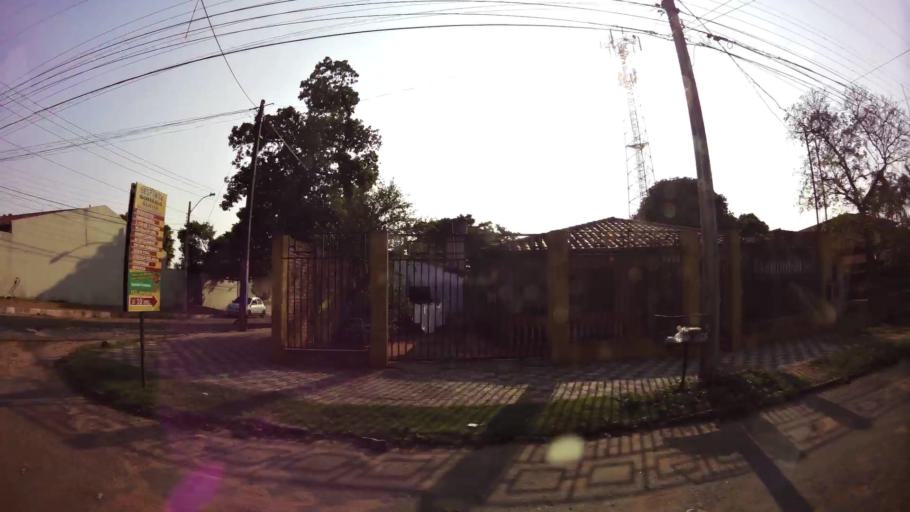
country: PY
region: Central
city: Lambare
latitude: -25.3457
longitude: -57.5961
